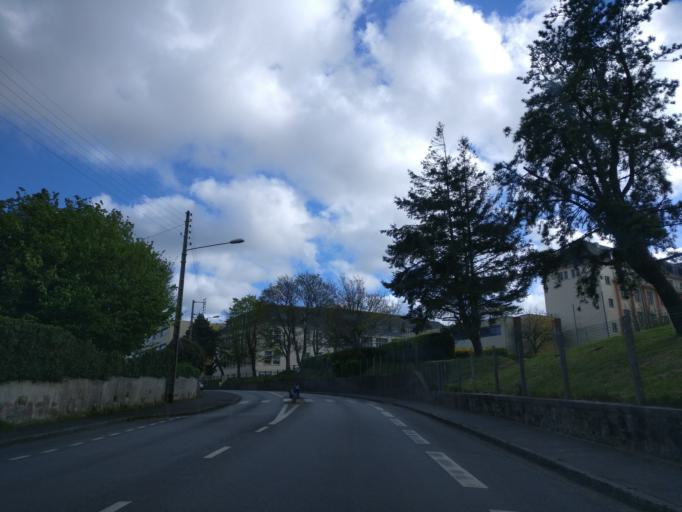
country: FR
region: Brittany
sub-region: Departement du Finistere
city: Brest
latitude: 48.4044
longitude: -4.4579
